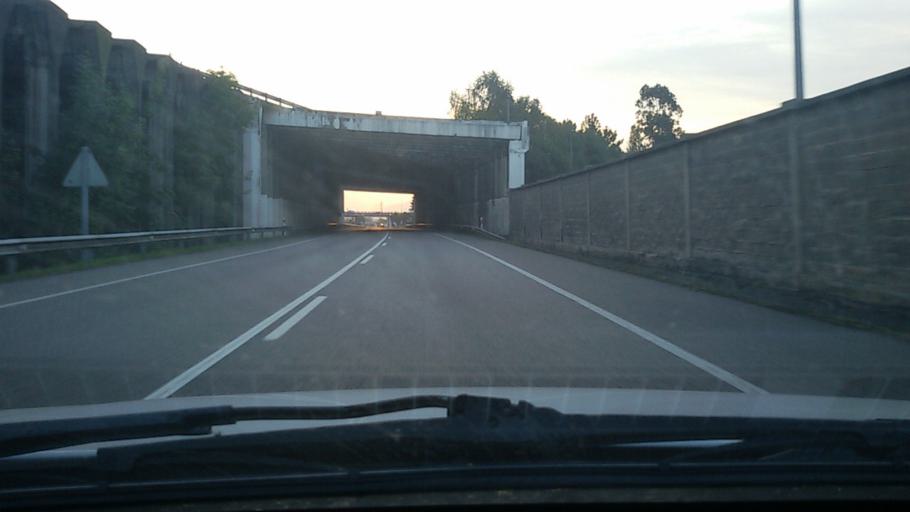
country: ES
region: Asturias
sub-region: Province of Asturias
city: Norena
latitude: 43.3820
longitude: -5.7314
